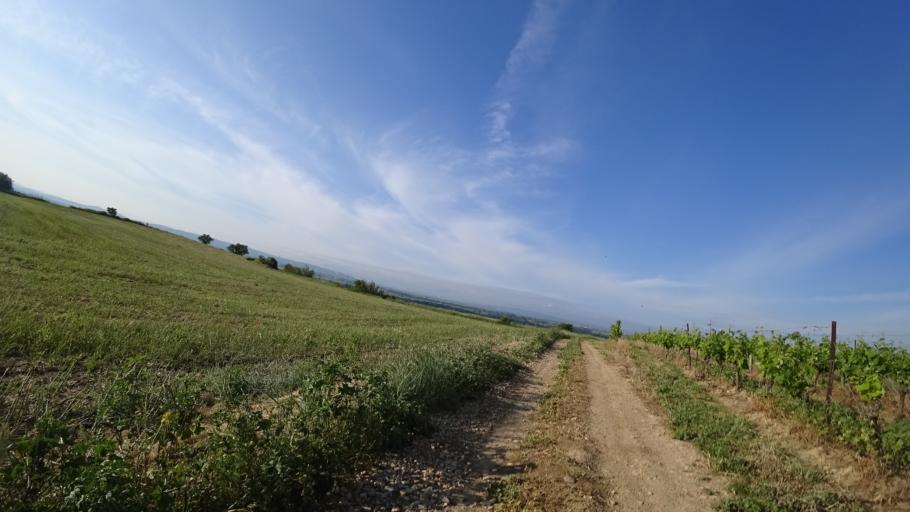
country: FR
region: Languedoc-Roussillon
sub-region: Departement de l'Aude
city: Canet
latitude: 43.2553
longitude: 2.8154
